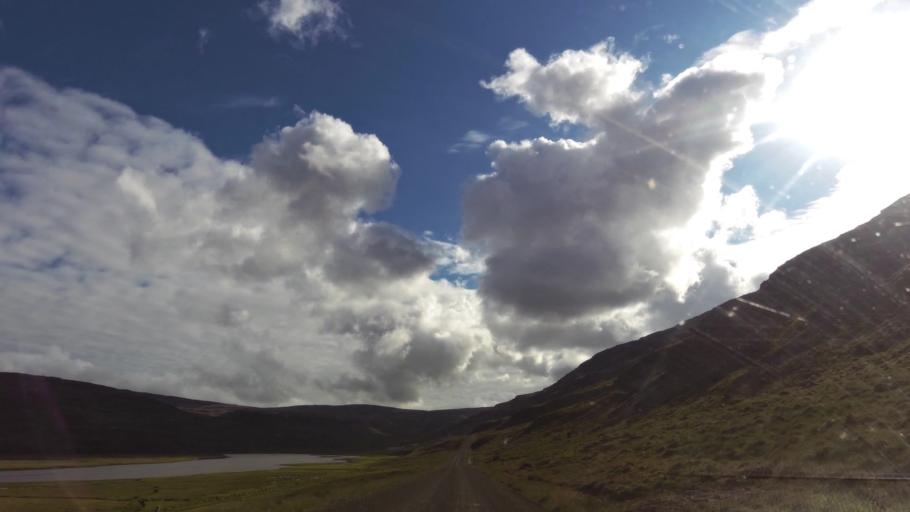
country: IS
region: West
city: Olafsvik
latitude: 65.5728
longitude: -24.1596
